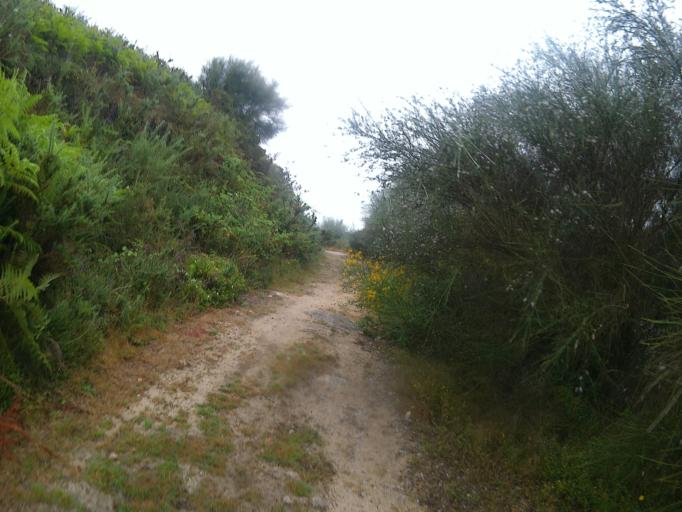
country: PT
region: Viana do Castelo
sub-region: Ponte de Lima
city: Ponte de Lima
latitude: 41.7166
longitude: -8.6030
